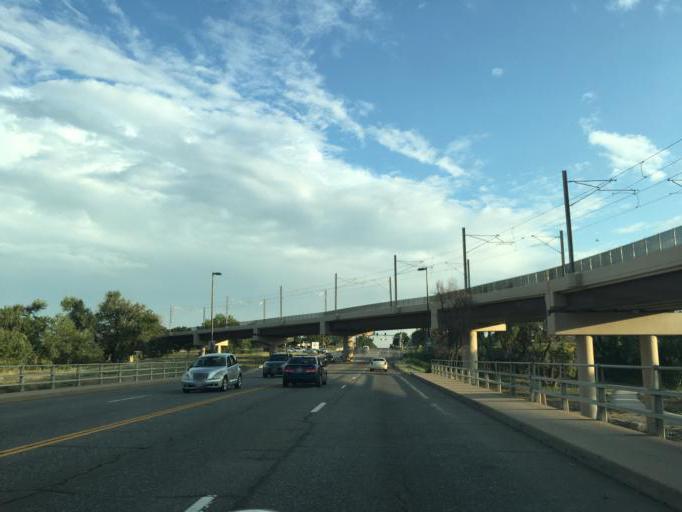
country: US
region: Colorado
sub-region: Adams County
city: Aurora
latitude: 39.7568
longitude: -104.8469
